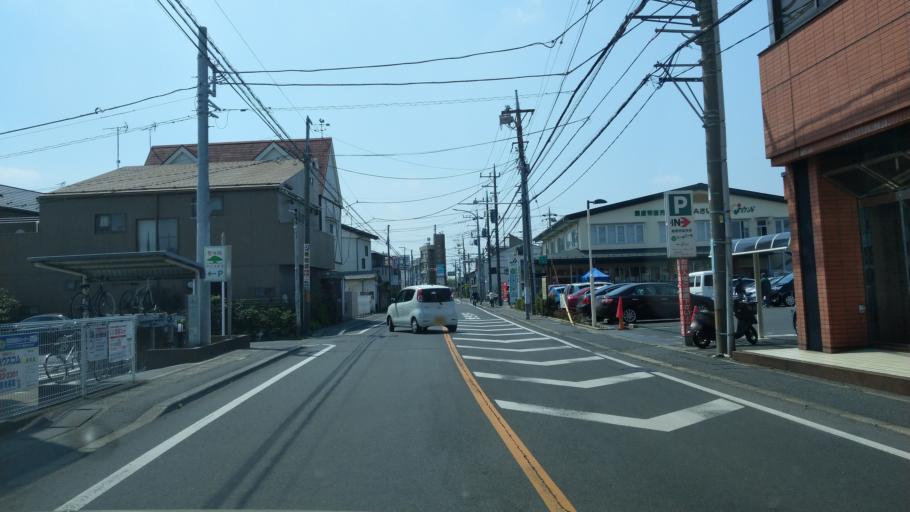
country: JP
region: Saitama
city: Yono
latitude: 35.8829
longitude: 139.6554
